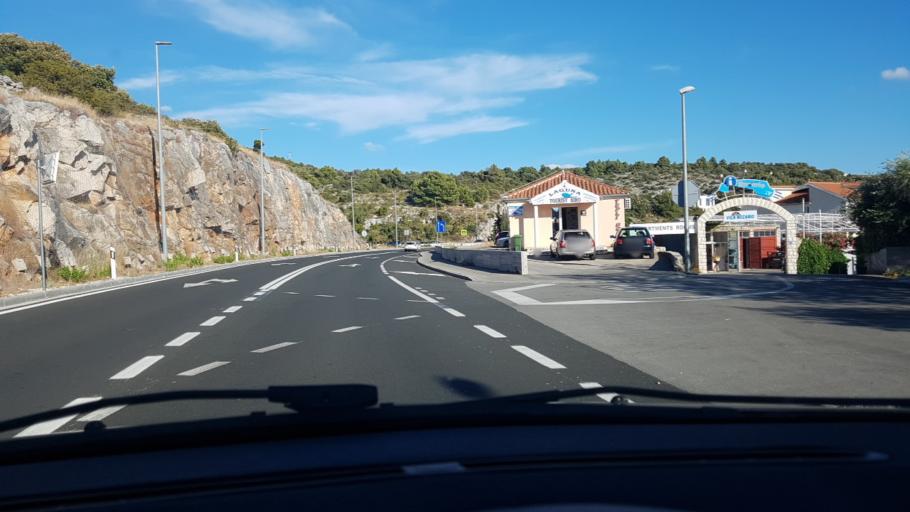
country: HR
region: Sibensko-Kniniska
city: Primosten
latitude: 43.5996
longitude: 15.9243
